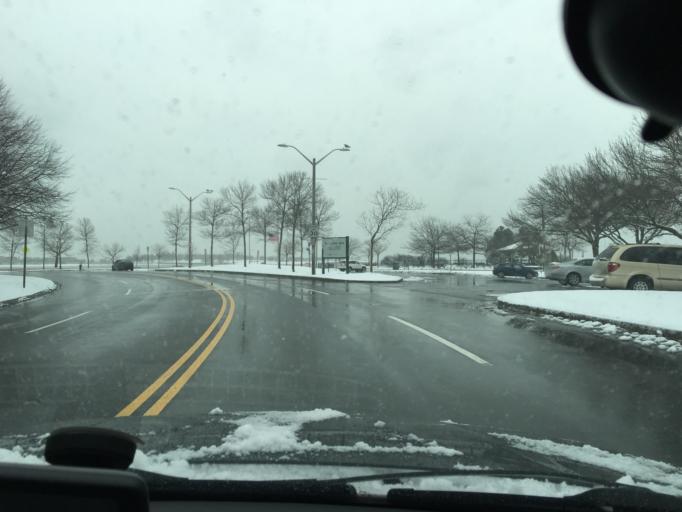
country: US
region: Massachusetts
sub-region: Suffolk County
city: South Boston
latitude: 42.3331
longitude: -71.0239
